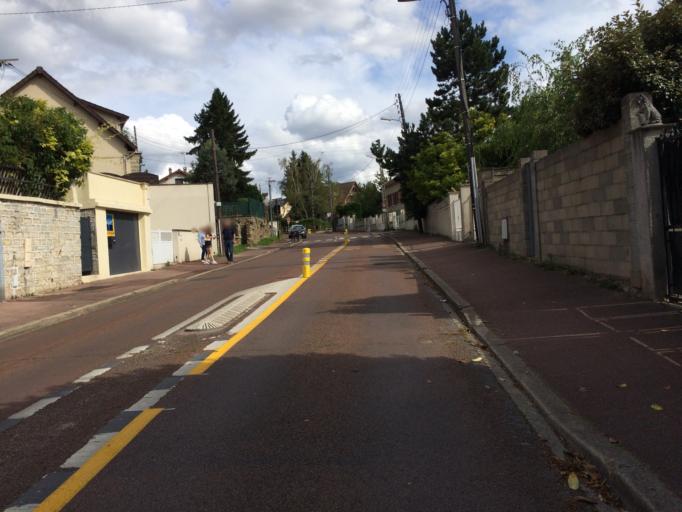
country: FR
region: Ile-de-France
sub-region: Departement de l'Essonne
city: Morangis
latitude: 48.6974
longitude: 2.3268
